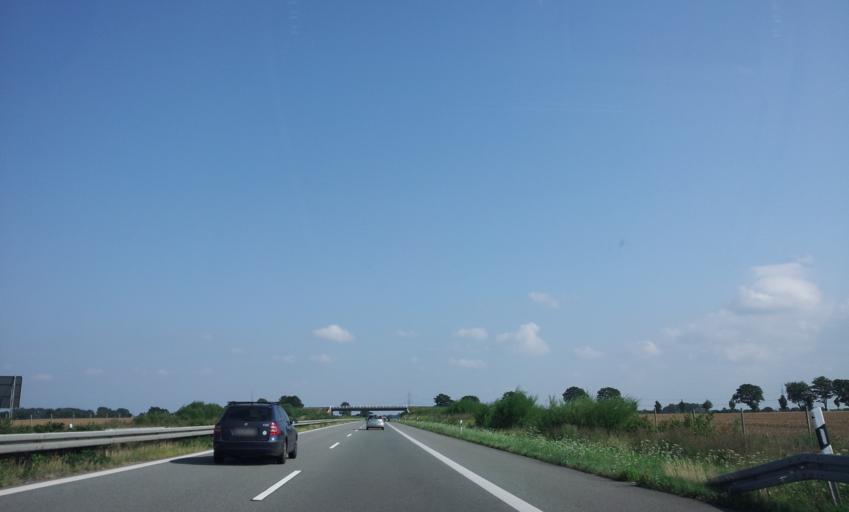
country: DE
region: Mecklenburg-Vorpommern
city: Dersekow
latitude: 54.0501
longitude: 13.2535
